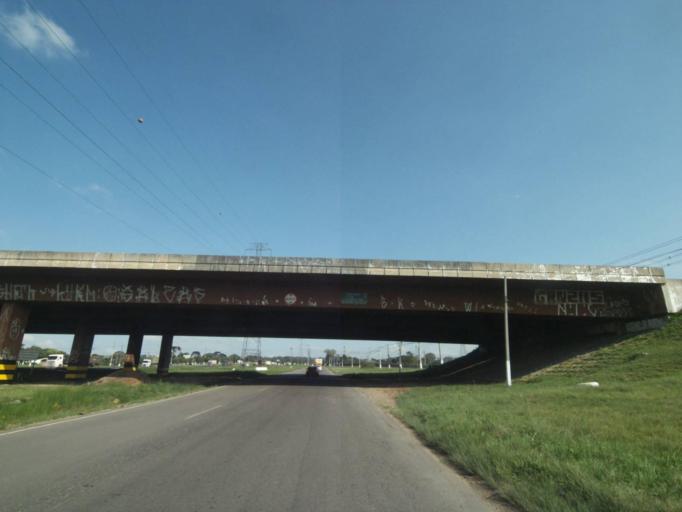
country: BR
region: Parana
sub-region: Araucaria
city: Araucaria
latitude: -25.5229
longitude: -49.3335
